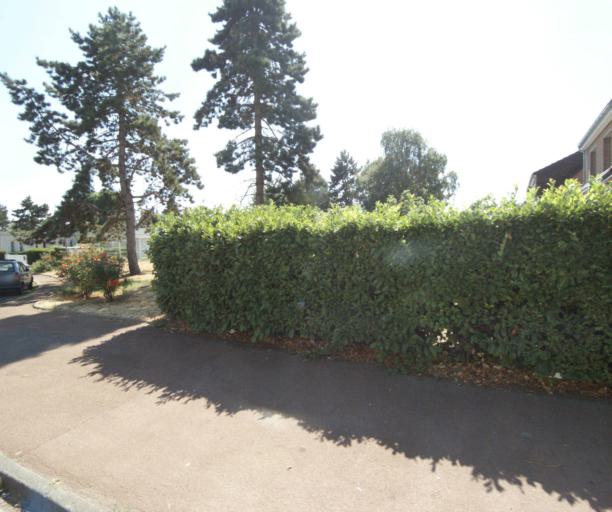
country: FR
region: Nord-Pas-de-Calais
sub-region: Departement du Nord
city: Wattrelos
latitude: 50.6946
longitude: 3.2076
